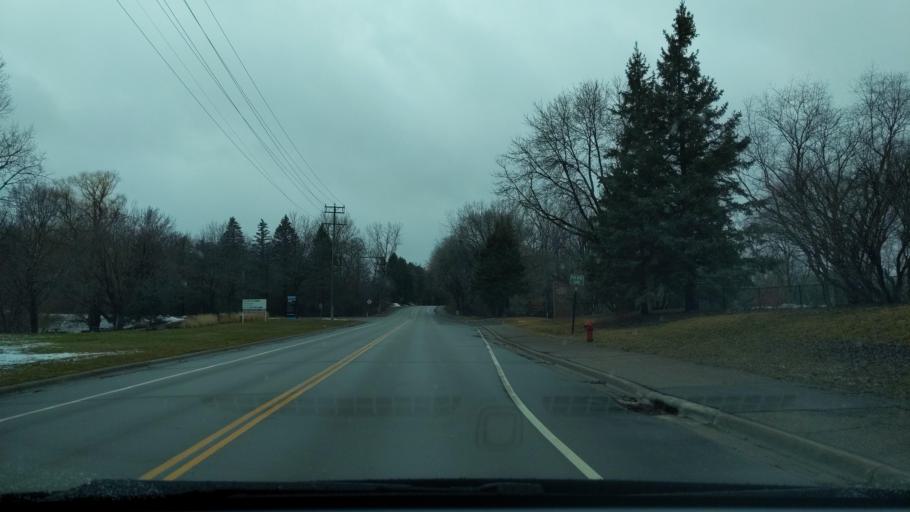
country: US
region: Minnesota
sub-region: Hennepin County
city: Hopkins
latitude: 44.9015
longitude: -93.4419
